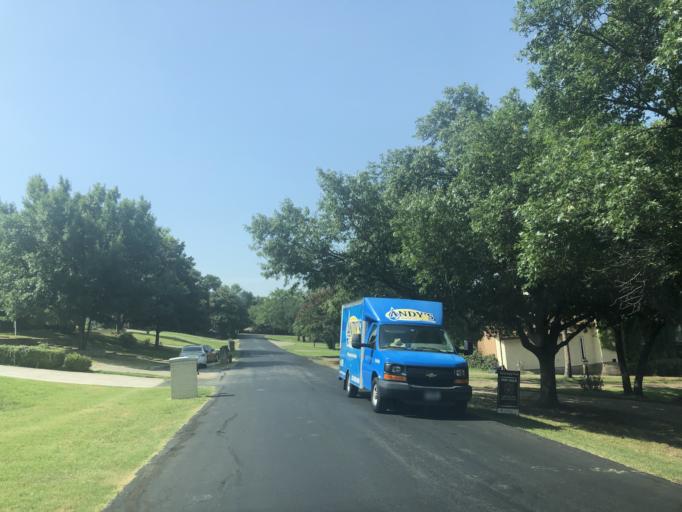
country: US
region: Texas
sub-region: Dallas County
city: Grand Prairie
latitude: 32.7696
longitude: -97.0345
